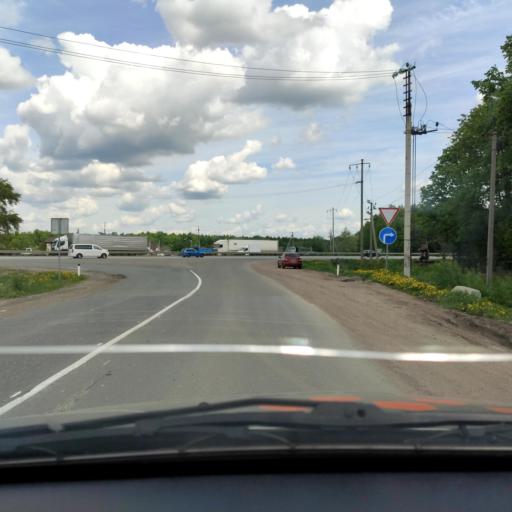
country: RU
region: Bashkortostan
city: Avdon
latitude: 54.6577
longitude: 55.7017
